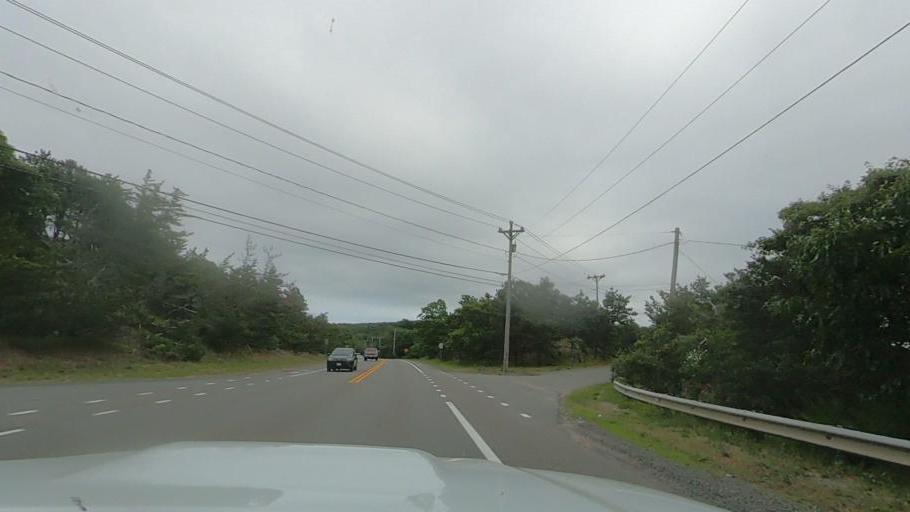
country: US
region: Massachusetts
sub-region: Barnstable County
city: Truro
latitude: 42.0086
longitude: -70.0659
